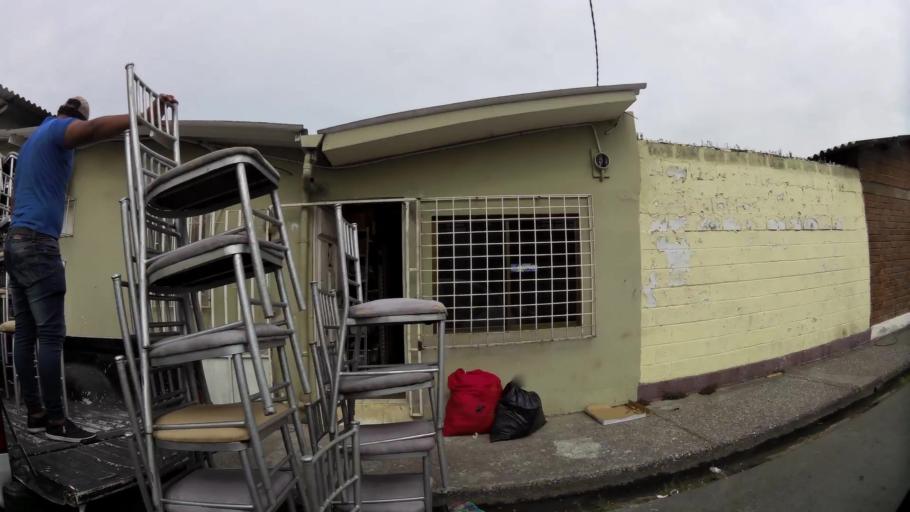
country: EC
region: Guayas
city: Eloy Alfaro
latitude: -2.1366
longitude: -79.8949
